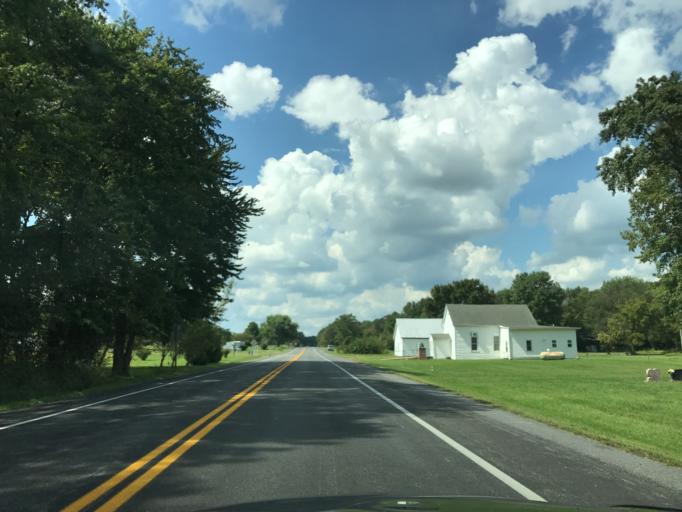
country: US
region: Maryland
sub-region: Caroline County
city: Greensboro
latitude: 39.1450
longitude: -75.8672
